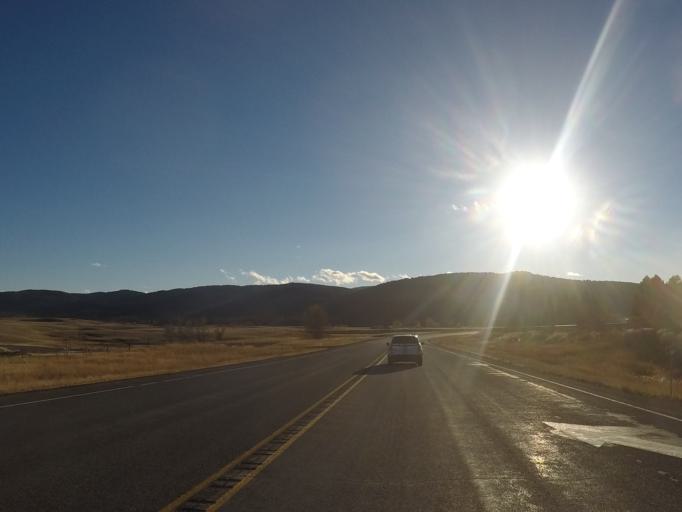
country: US
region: Montana
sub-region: Lewis and Clark County
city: Helena West Side
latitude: 46.5587
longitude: -112.3884
